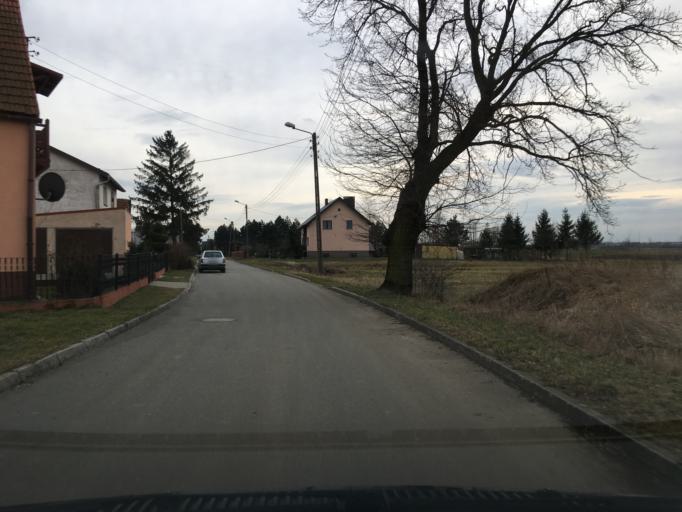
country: PL
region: Opole Voivodeship
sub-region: Powiat kedzierzynsko-kozielski
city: Wiekszyce
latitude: 50.3590
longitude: 18.1181
